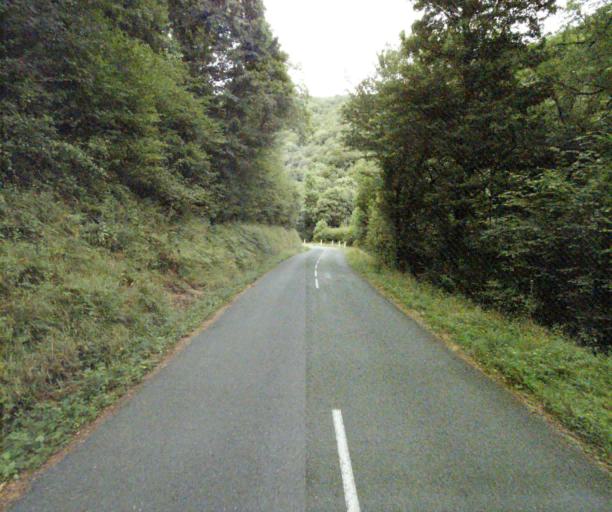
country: FR
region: Midi-Pyrenees
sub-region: Departement du Tarn
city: Soreze
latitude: 43.4362
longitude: 2.0850
